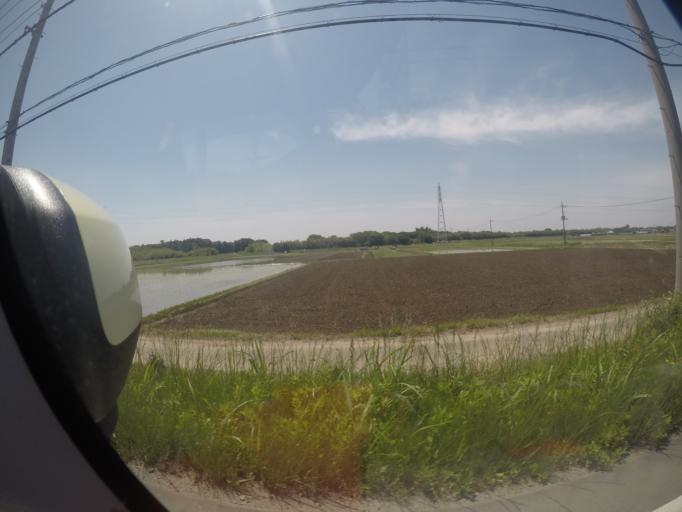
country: JP
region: Ibaraki
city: Tsukuba
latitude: 36.2112
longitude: 140.0710
